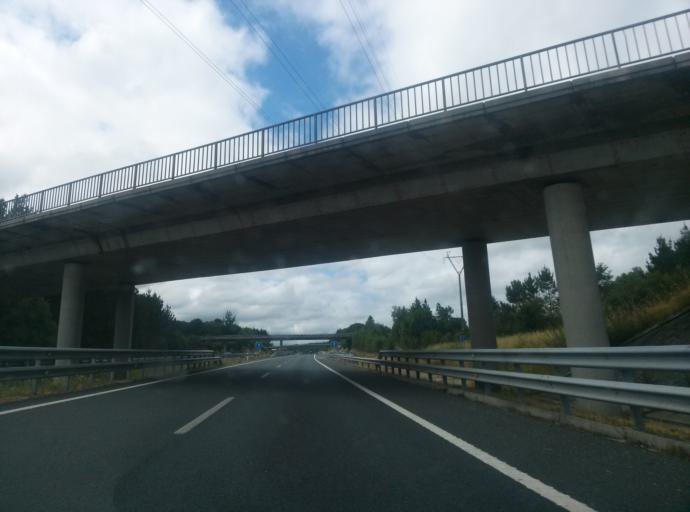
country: ES
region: Galicia
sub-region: Provincia de Lugo
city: Begonte
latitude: 43.1587
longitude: -7.6852
